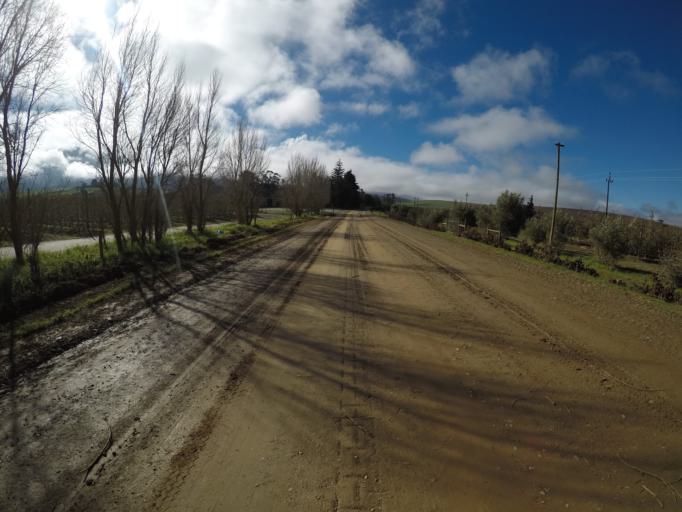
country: ZA
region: Western Cape
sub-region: Overberg District Municipality
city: Caledon
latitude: -34.1119
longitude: 19.7464
